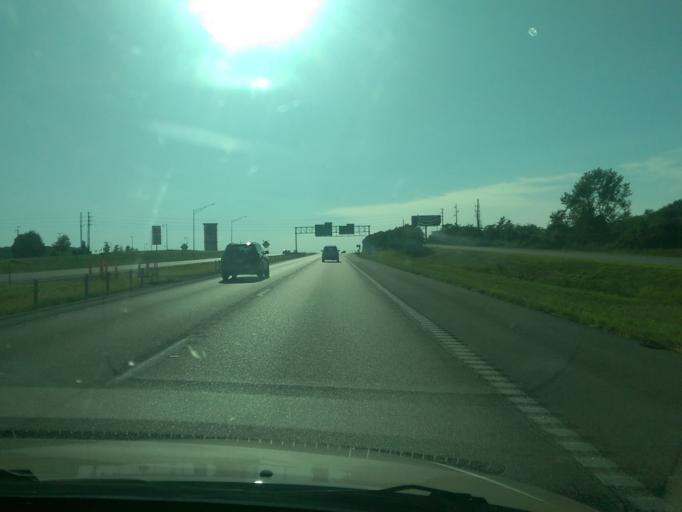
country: US
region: Missouri
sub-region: Jackson County
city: Blue Springs
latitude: 39.0266
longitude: -94.2404
